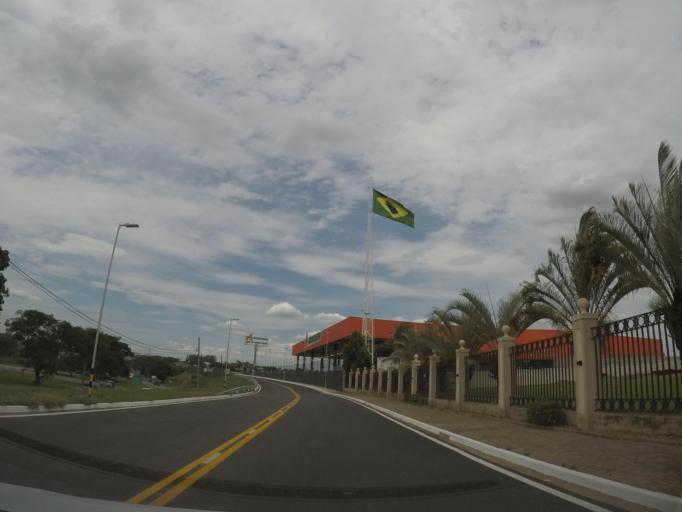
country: BR
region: Sao Paulo
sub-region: Sumare
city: Sumare
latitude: -22.8015
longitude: -47.2381
